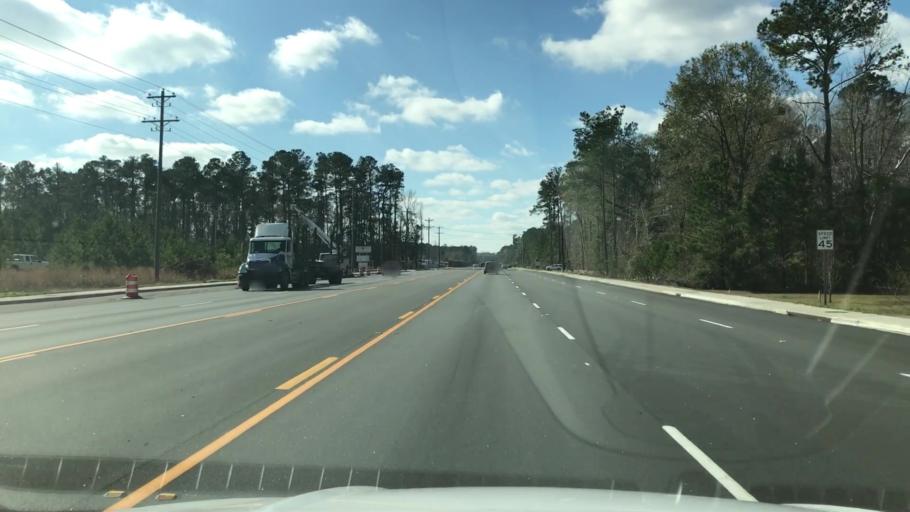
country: US
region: South Carolina
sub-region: Horry County
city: Socastee
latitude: 33.6492
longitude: -79.0230
